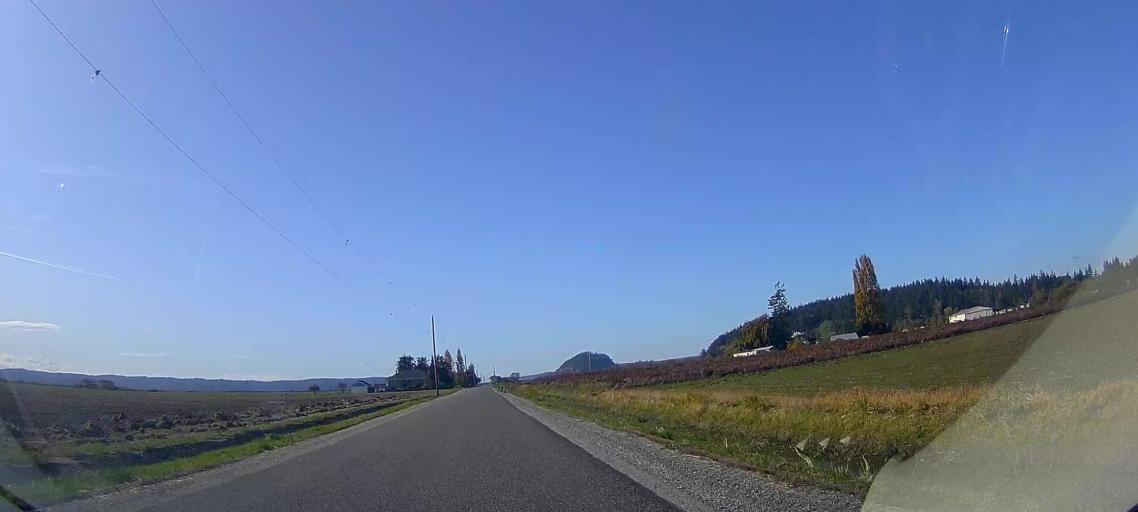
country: US
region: Washington
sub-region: Skagit County
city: Mount Vernon
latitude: 48.3557
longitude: -122.4400
